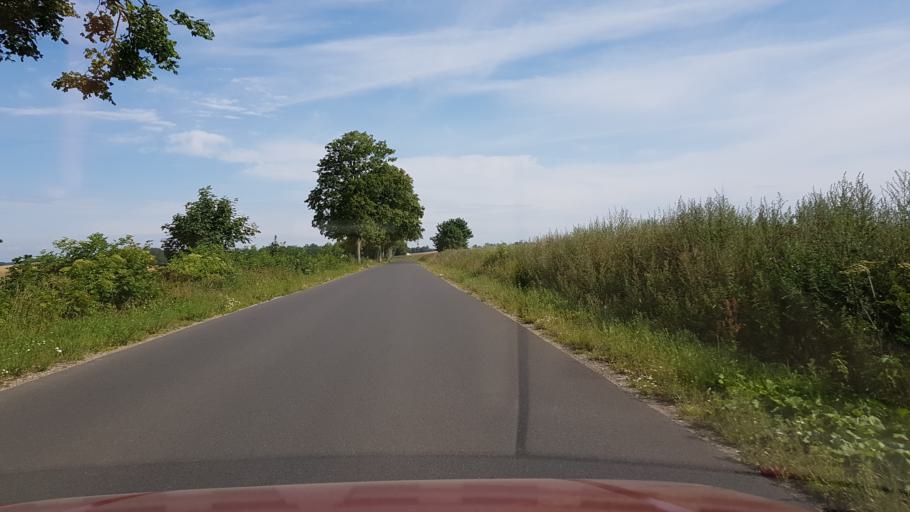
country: PL
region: West Pomeranian Voivodeship
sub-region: Powiat koszalinski
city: Polanow
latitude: 54.1427
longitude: 16.6217
